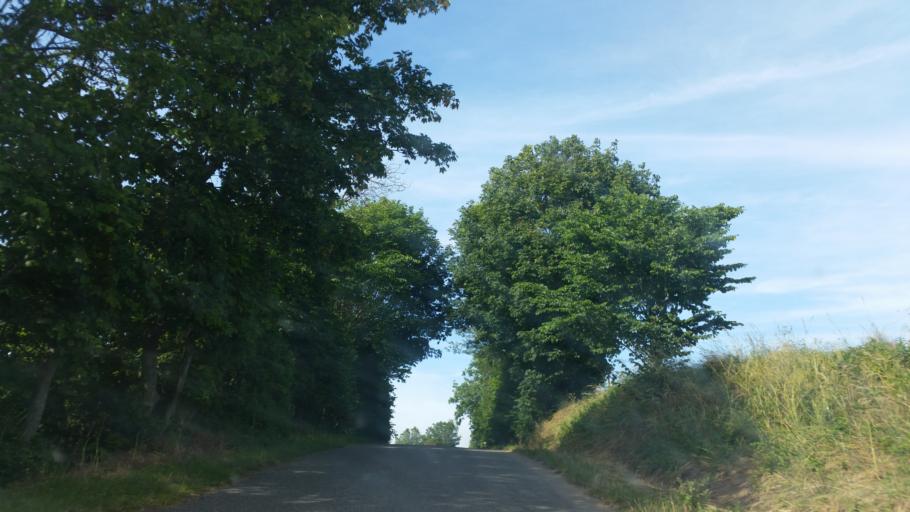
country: DK
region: Central Jutland
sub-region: Samso Kommune
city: Tranebjerg
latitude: 55.8337
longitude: 10.5351
